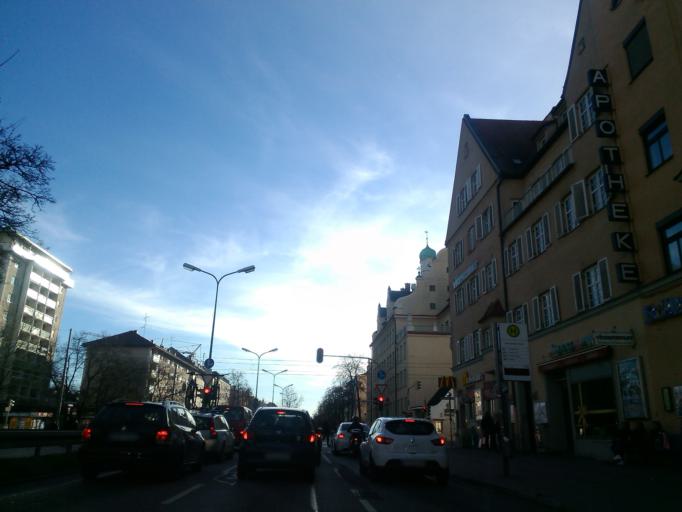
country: DE
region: Bavaria
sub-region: Upper Bavaria
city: Pasing
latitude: 48.1401
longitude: 11.5031
